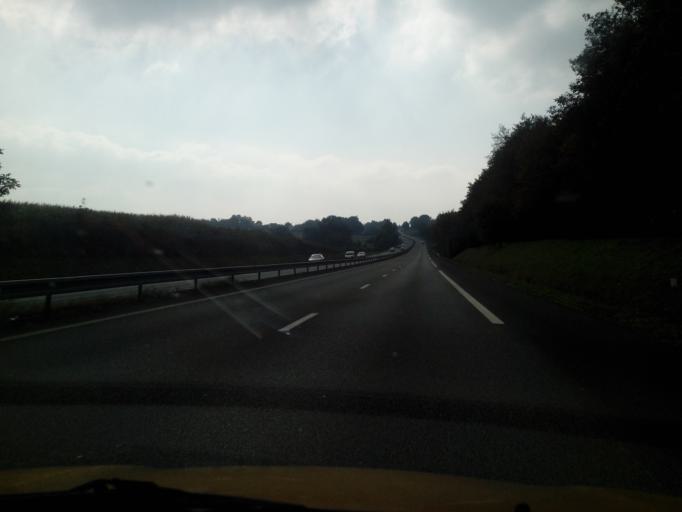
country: FR
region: Brittany
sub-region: Departement du Morbihan
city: Ploermel
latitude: 47.8793
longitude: -2.4170
